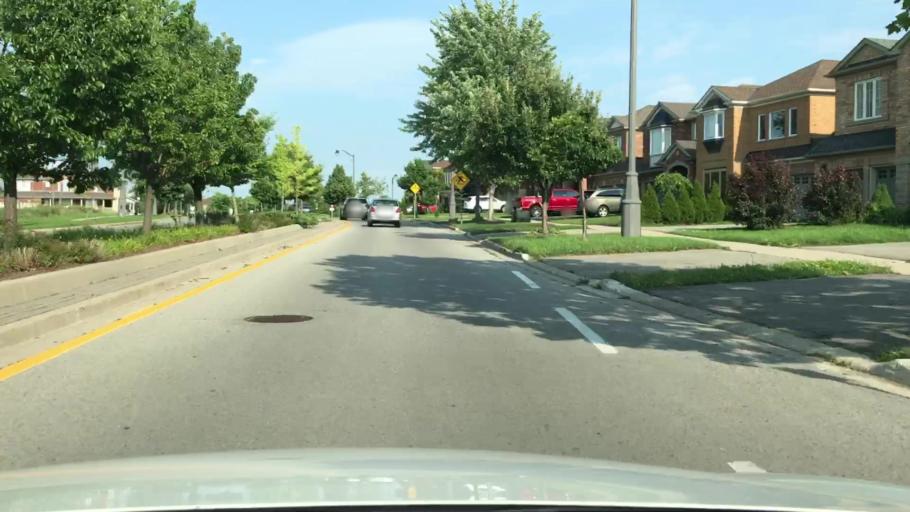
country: CA
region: Ontario
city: Newmarket
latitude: 44.0127
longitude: -79.4439
